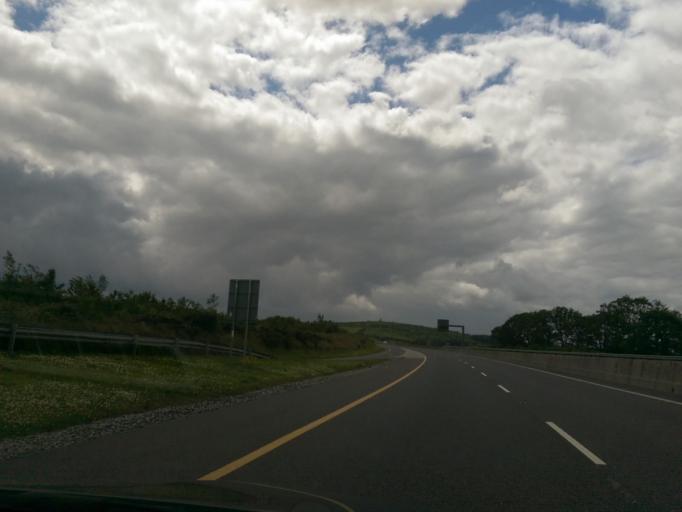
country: IE
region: Munster
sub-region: County Cork
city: Mitchelstown
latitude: 52.2364
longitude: -8.2826
